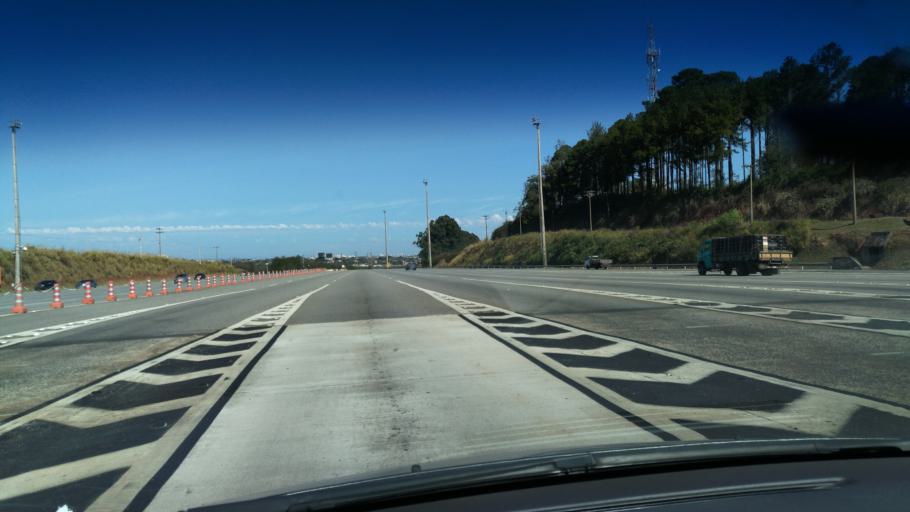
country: BR
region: Sao Paulo
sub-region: Jaguariuna
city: Jaguariuna
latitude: -22.7713
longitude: -47.0221
